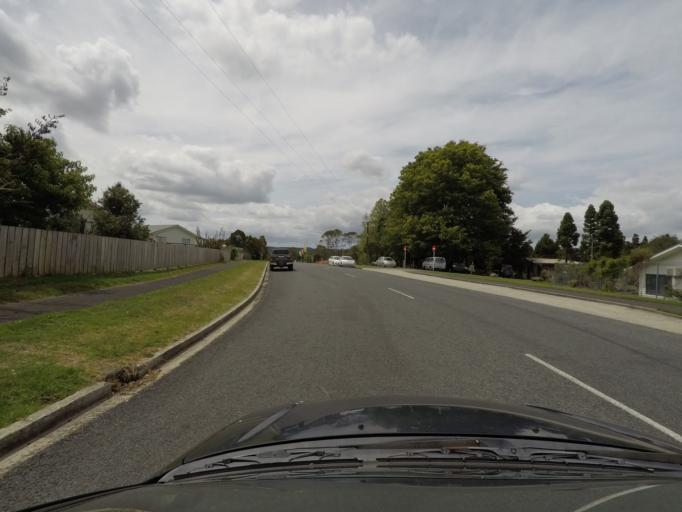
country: NZ
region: Northland
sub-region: Whangarei
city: Whangarei
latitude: -35.6851
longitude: 174.3344
